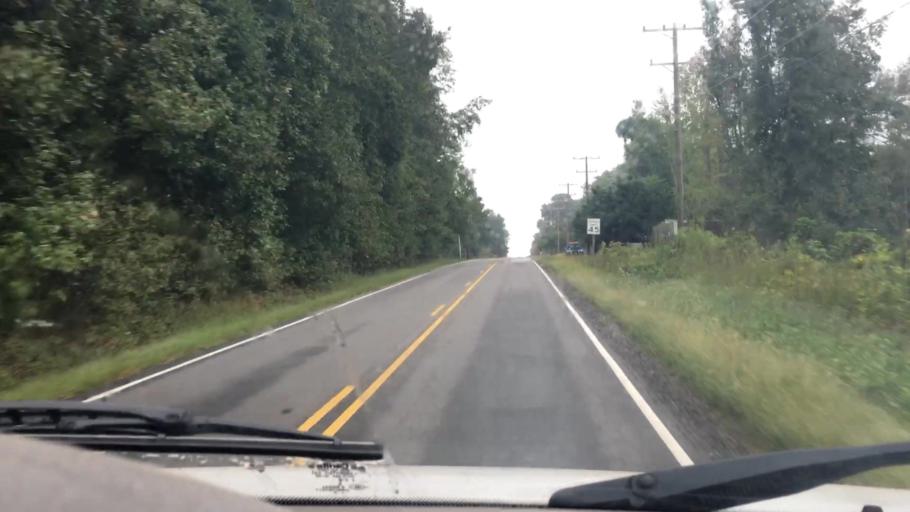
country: US
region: North Carolina
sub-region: Iredell County
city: Mooresville
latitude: 35.6265
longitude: -80.7807
